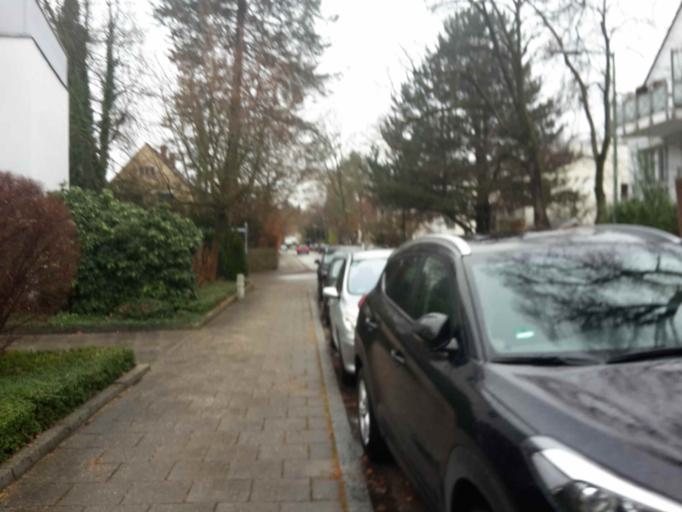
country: DE
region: Bavaria
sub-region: Upper Bavaria
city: Pullach im Isartal
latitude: 48.0813
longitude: 11.5200
